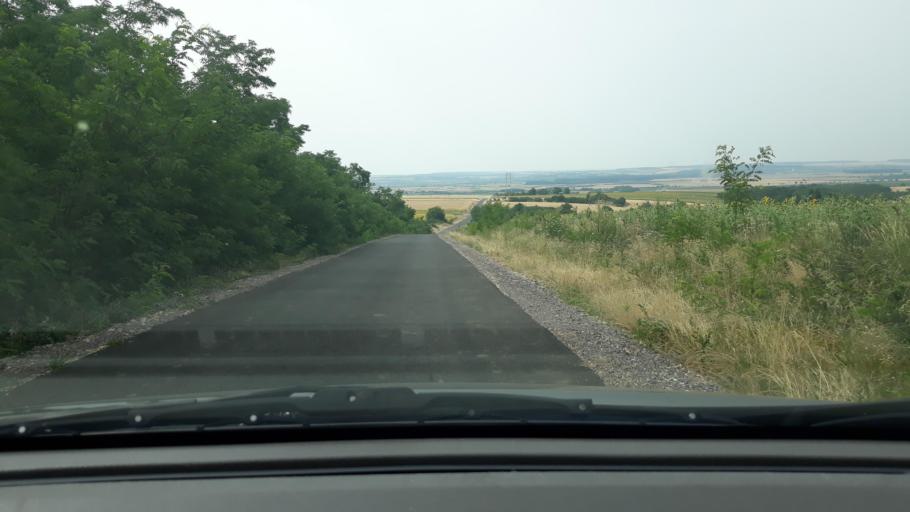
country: RO
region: Bihor
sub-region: Comuna Chislaz
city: Misca
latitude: 47.2622
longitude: 22.2917
